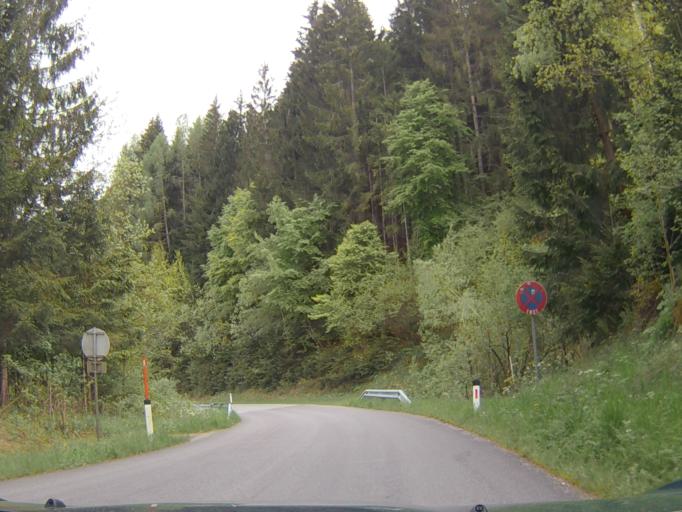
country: AT
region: Carinthia
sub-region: Politischer Bezirk Villach Land
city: Stockenboi
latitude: 46.7379
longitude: 13.5683
